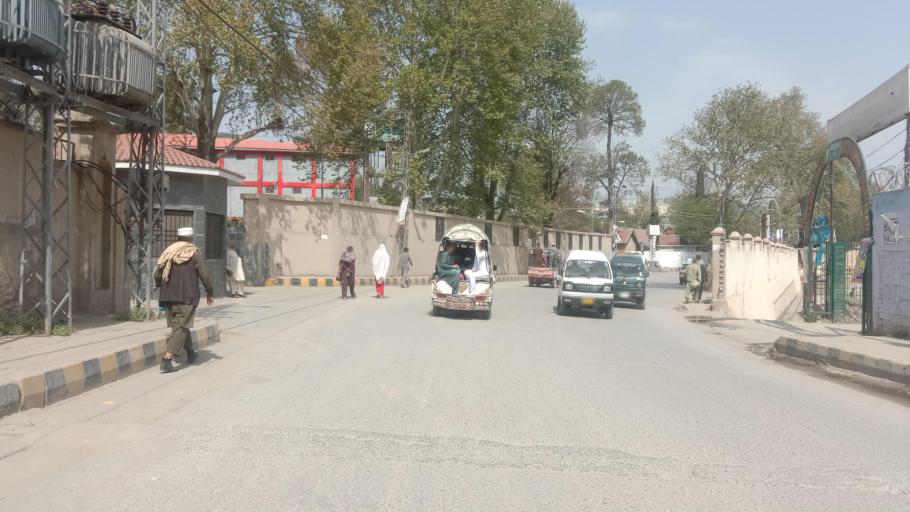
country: PK
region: Khyber Pakhtunkhwa
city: Abbottabad
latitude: 34.1429
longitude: 73.2120
